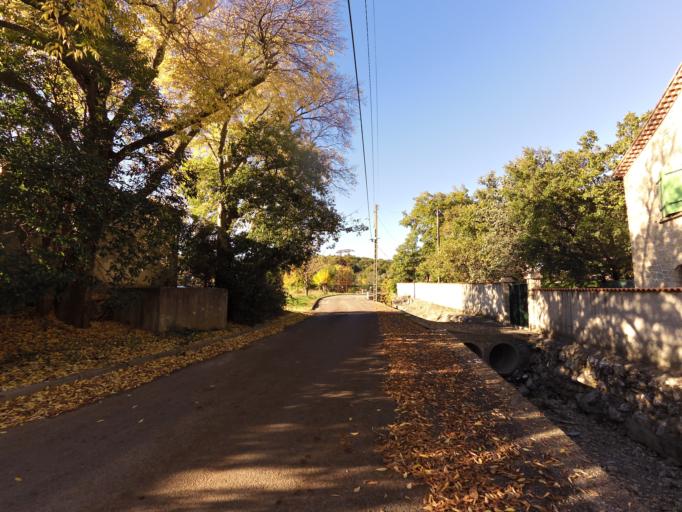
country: FR
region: Languedoc-Roussillon
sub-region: Departement du Gard
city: Sauve
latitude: 43.9891
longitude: 3.9506
